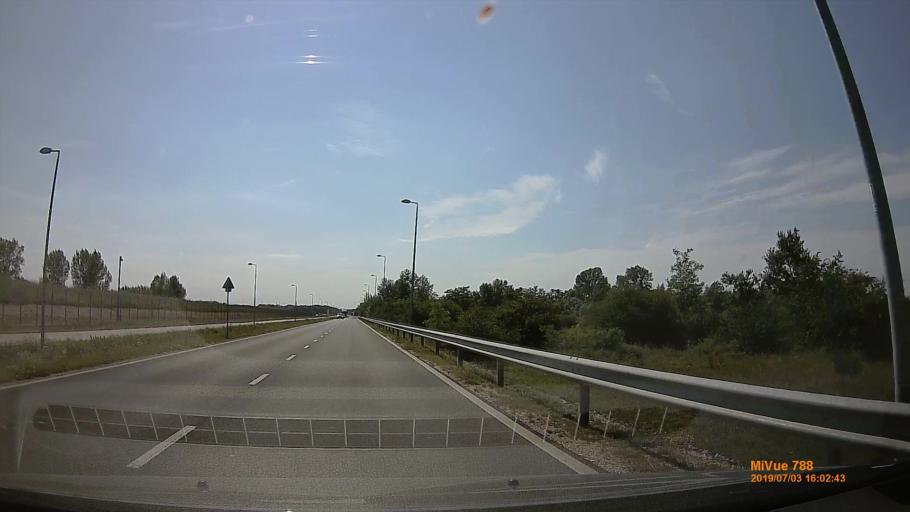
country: HU
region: Gyor-Moson-Sopron
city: Gyor
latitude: 47.7064
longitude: 17.7030
